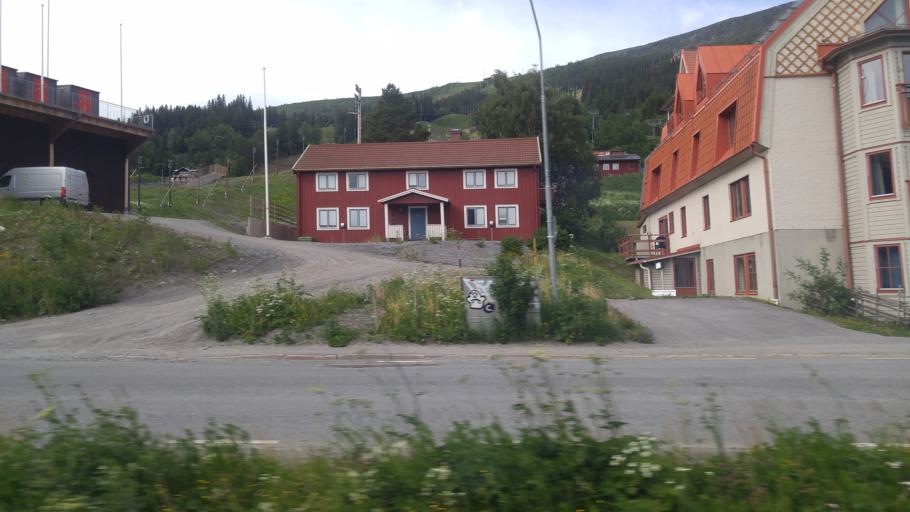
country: SE
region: Jaemtland
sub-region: Are Kommun
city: Are
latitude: 63.4030
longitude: 13.0574
